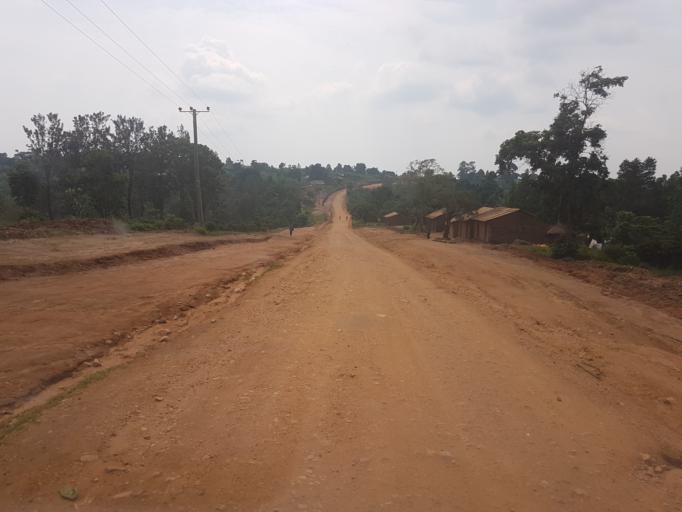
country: UG
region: Western Region
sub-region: Kanungu District
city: Ntungamo
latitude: -0.8199
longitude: 29.7077
